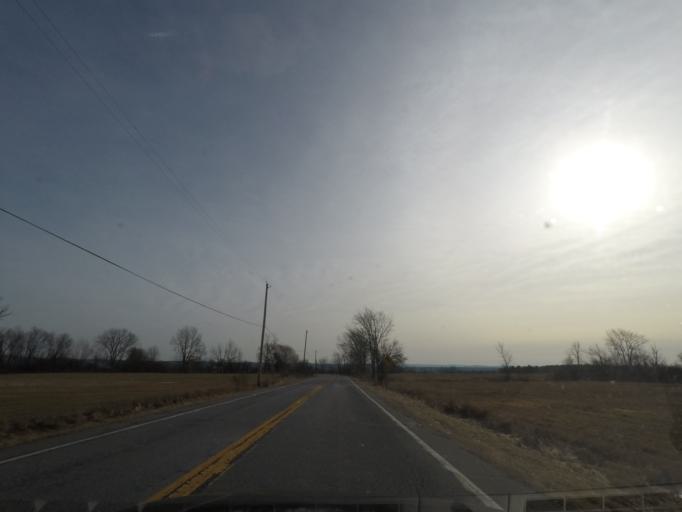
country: US
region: New York
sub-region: Saratoga County
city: Stillwater
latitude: 42.9837
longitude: -73.6481
